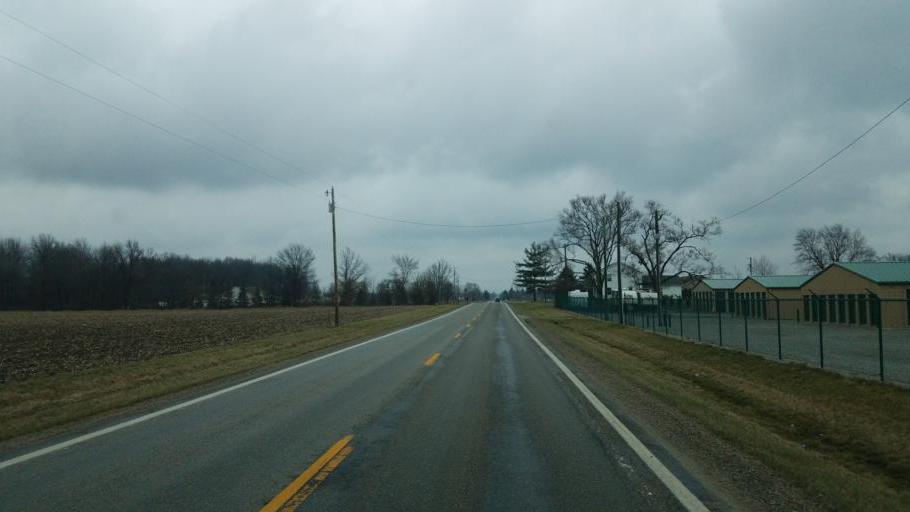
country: US
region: Ohio
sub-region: Delaware County
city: Ashley
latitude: 40.4077
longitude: -82.9229
